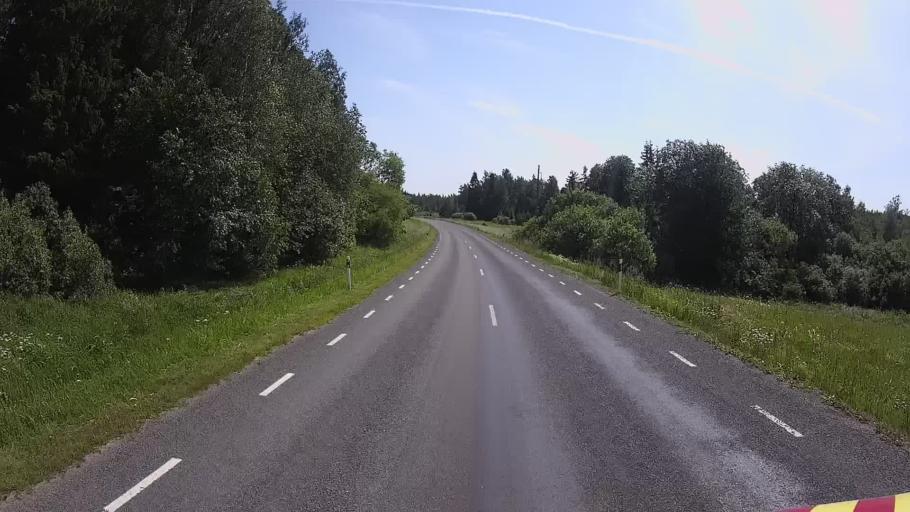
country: EE
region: Viljandimaa
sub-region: Karksi vald
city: Karksi-Nuia
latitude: 58.0909
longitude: 25.5582
